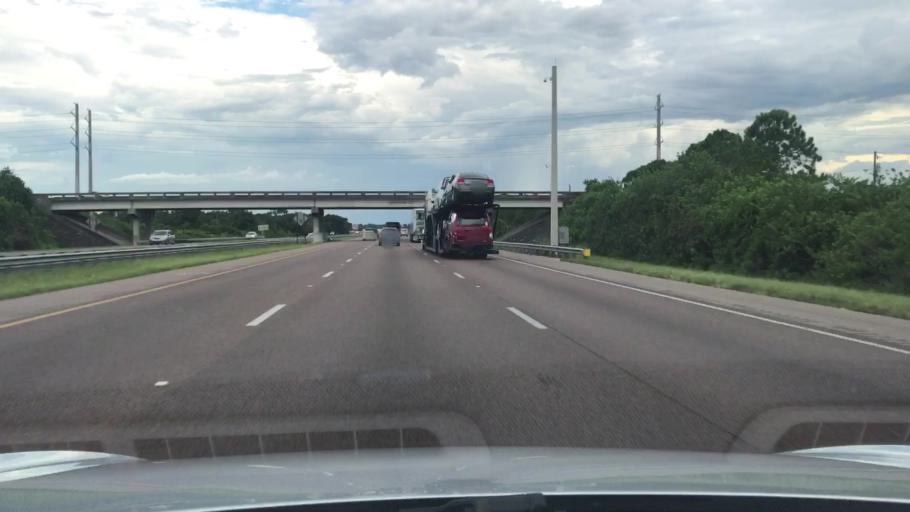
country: US
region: Florida
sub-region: Brevard County
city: Grant-Valkaria
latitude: 27.8747
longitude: -80.5917
